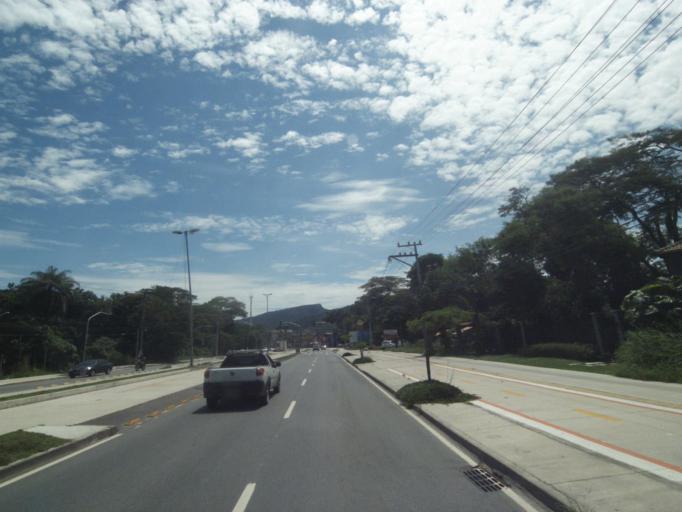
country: BR
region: Rio de Janeiro
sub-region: Niteroi
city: Niteroi
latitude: -22.9487
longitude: -43.0293
